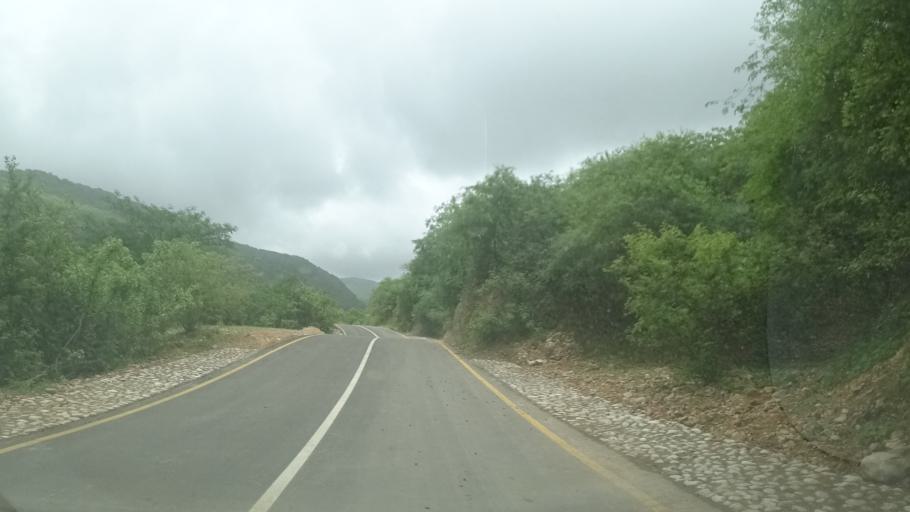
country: OM
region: Zufar
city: Salalah
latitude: 17.1023
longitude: 54.3477
